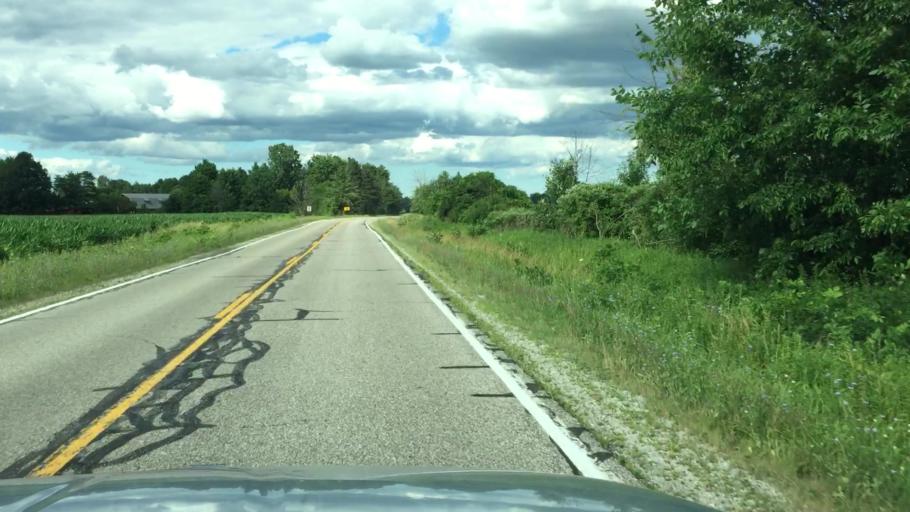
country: US
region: Michigan
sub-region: Saint Clair County
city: Capac
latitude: 43.1109
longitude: -82.9016
